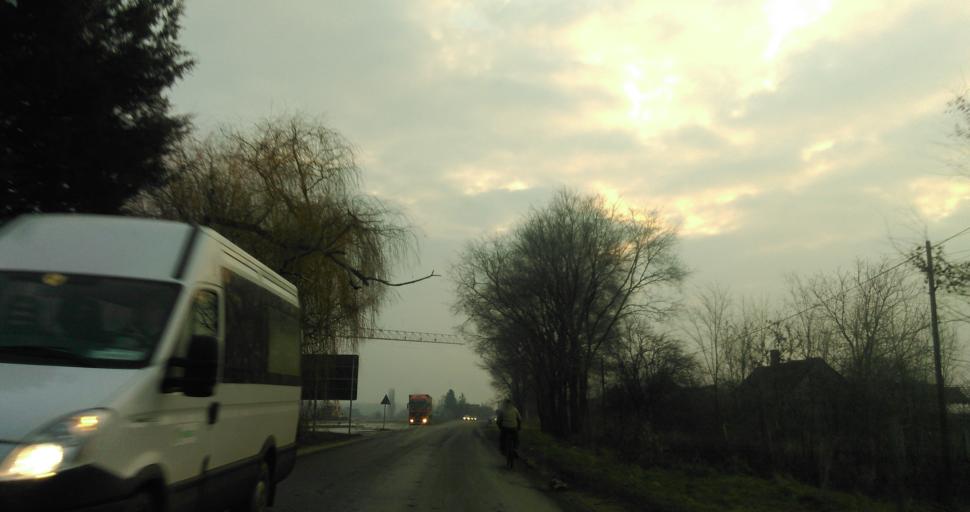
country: RS
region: Autonomna Pokrajina Vojvodina
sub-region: Juznobacki Okrug
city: Becej
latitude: 45.6003
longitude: 20.0412
